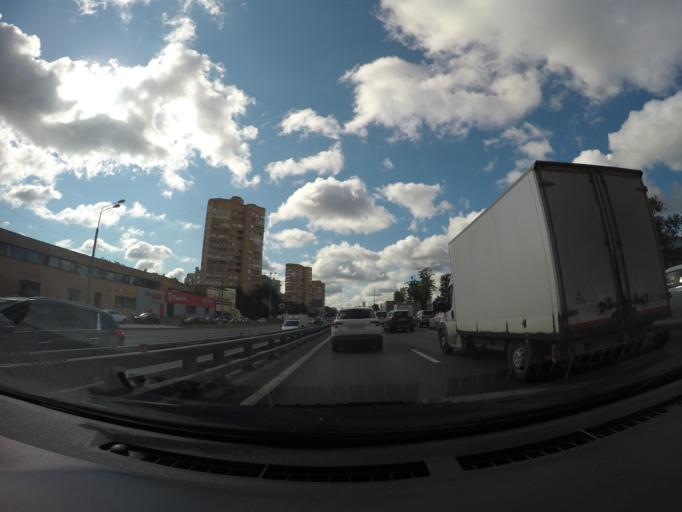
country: RU
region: Moskovskaya
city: Levoberezhnyy
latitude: 55.8489
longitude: 37.4747
